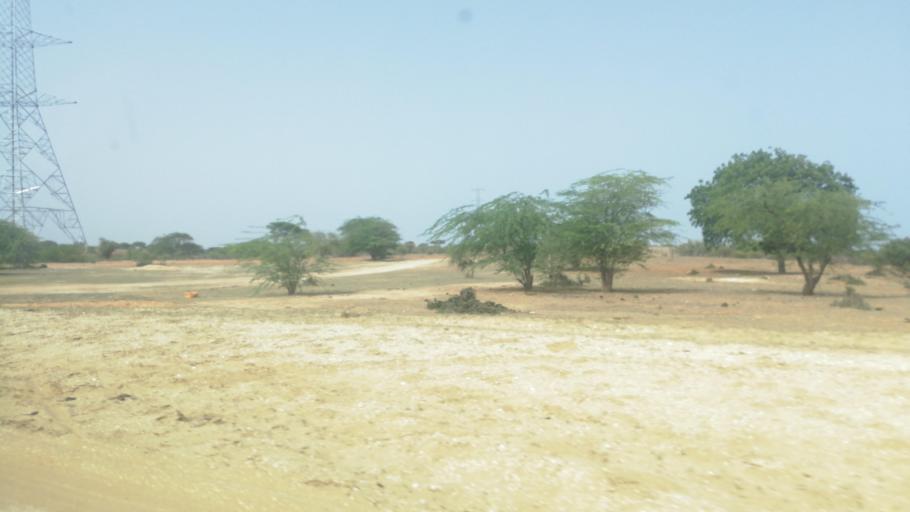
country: SN
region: Saint-Louis
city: Saint-Louis
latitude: 16.0809
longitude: -16.3617
